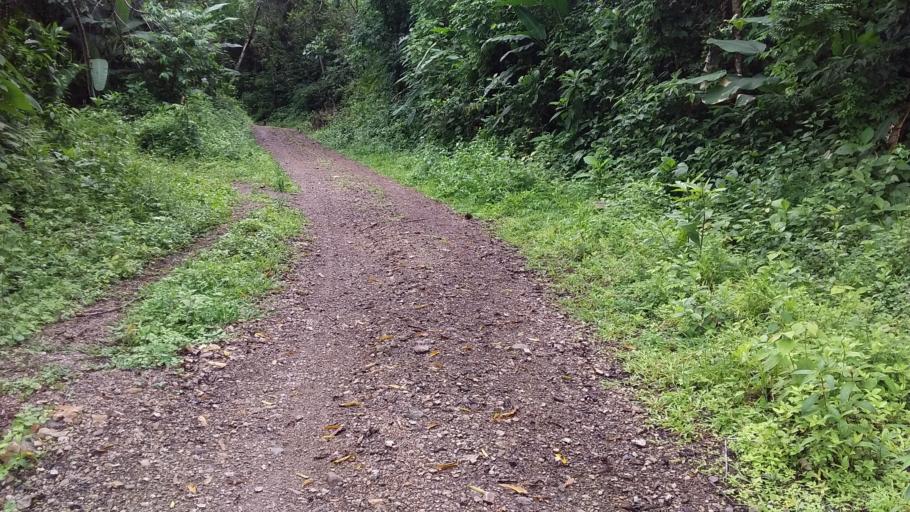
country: CO
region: Casanare
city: Nunchia
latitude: 5.6456
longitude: -72.2942
